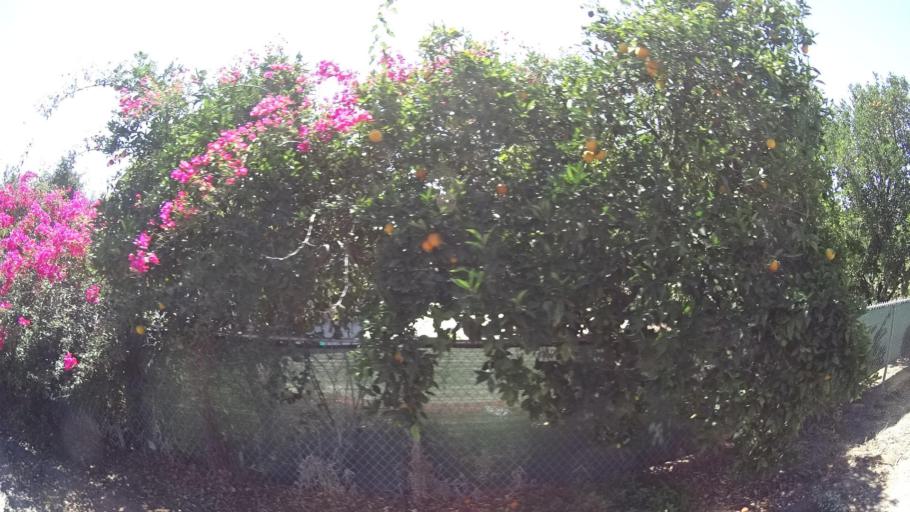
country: US
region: California
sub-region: San Diego County
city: Valley Center
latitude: 33.2737
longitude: -117.0072
